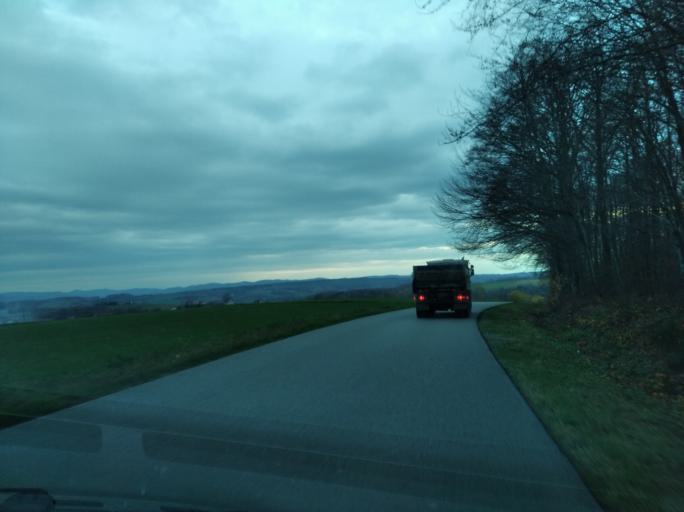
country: PL
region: Subcarpathian Voivodeship
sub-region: Powiat ropczycko-sedziszowski
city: Zagorzyce
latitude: 49.9418
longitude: 21.6934
